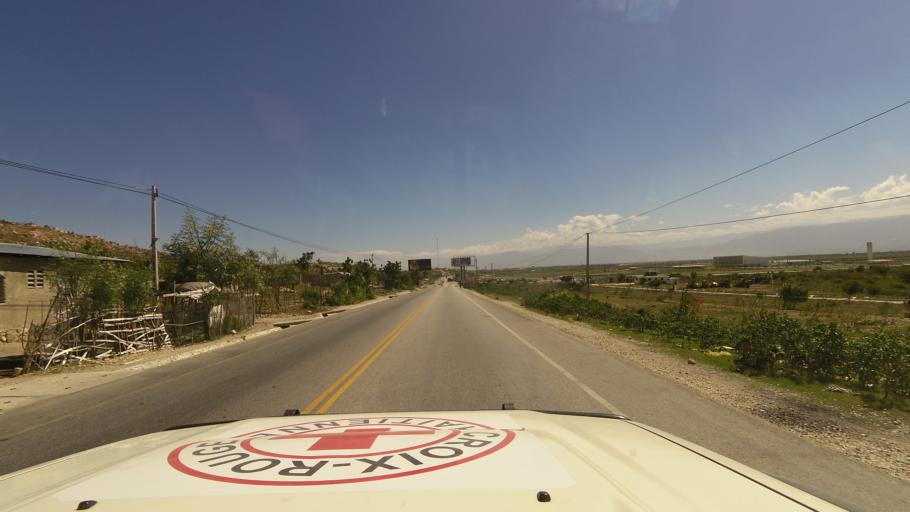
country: HT
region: Ouest
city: Croix des Bouquets
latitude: 18.6614
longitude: -72.2935
